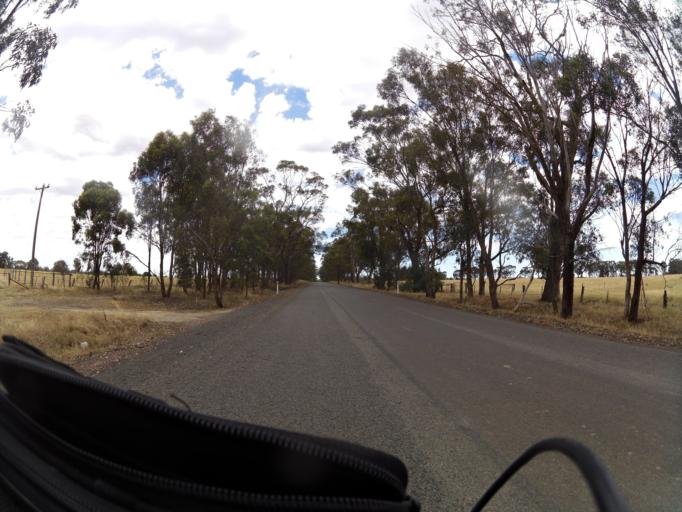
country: AU
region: Victoria
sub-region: Campaspe
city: Kyabram
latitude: -36.7352
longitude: 145.1438
